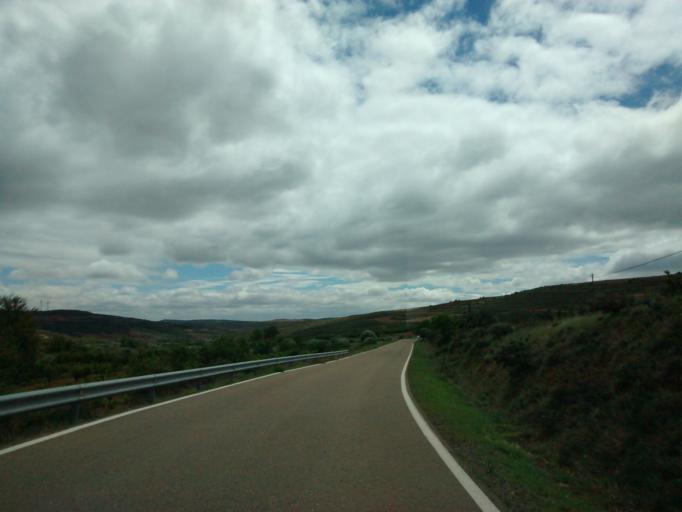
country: ES
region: Aragon
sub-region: Provincia de Zaragoza
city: Lituenigo
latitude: 41.8408
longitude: -1.7415
